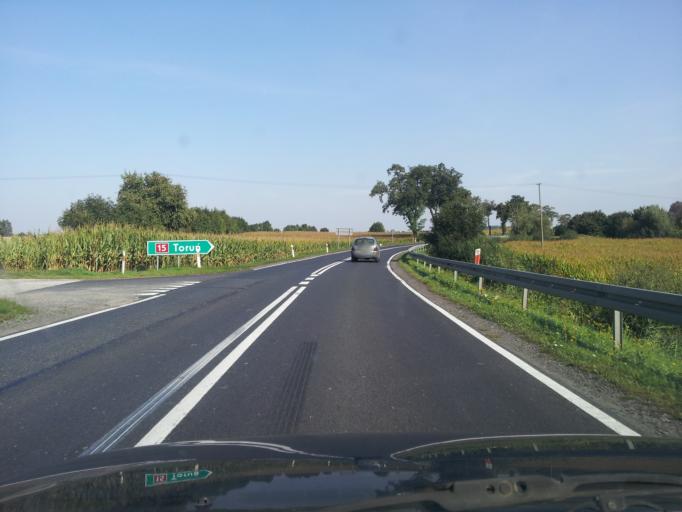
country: PL
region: Kujawsko-Pomorskie
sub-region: Powiat mogilenski
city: Mogilno
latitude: 52.6133
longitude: 17.9148
